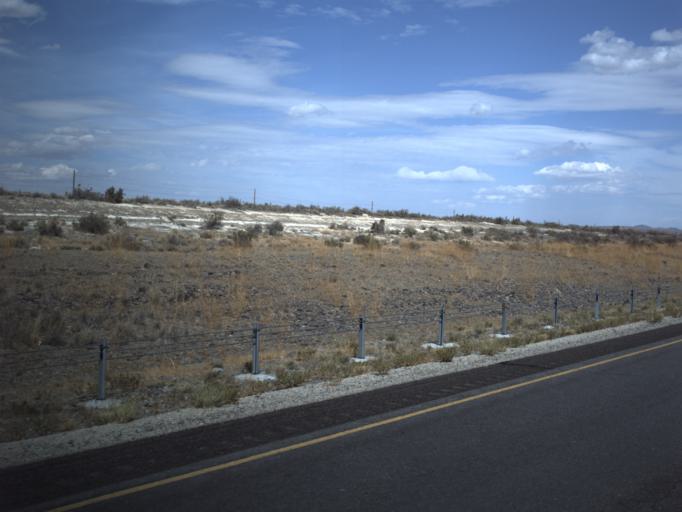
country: US
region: Utah
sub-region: Tooele County
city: Grantsville
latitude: 40.7260
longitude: -113.1341
